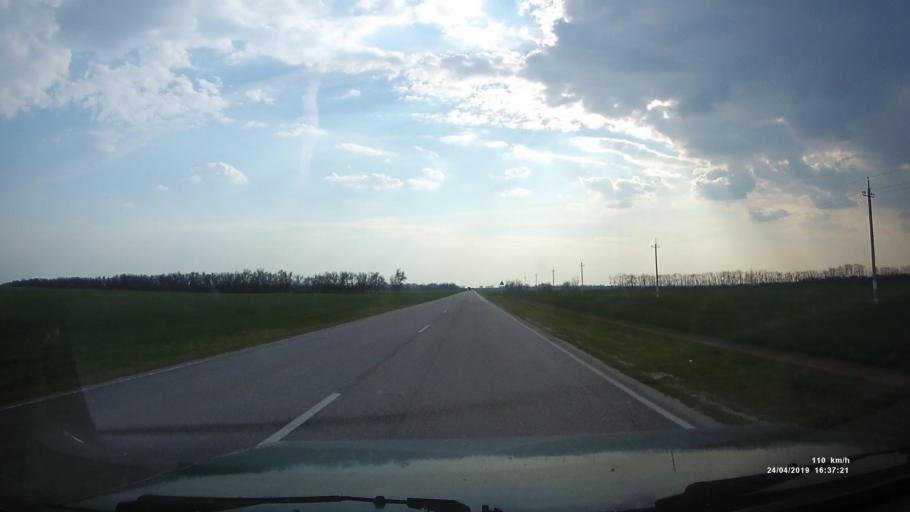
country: RU
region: Rostov
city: Gundorovskiy
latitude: 46.8574
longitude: 41.9370
